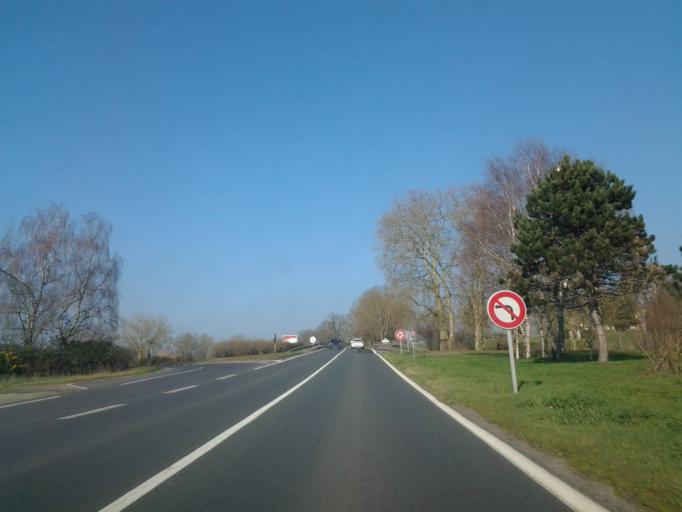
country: FR
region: Pays de la Loire
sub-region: Departement de la Vendee
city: Saint-Christophe-du-Ligneron
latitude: 46.8198
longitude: -1.7634
